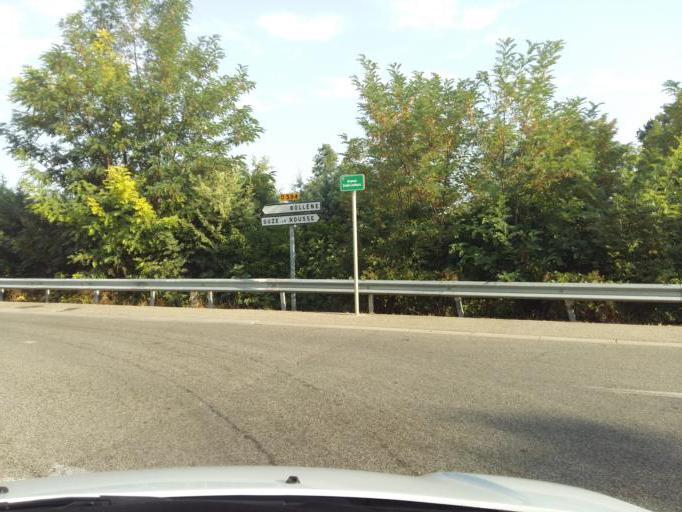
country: FR
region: Provence-Alpes-Cote d'Azur
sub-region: Departement du Vaucluse
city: Bollene
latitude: 44.2795
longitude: 4.7820
